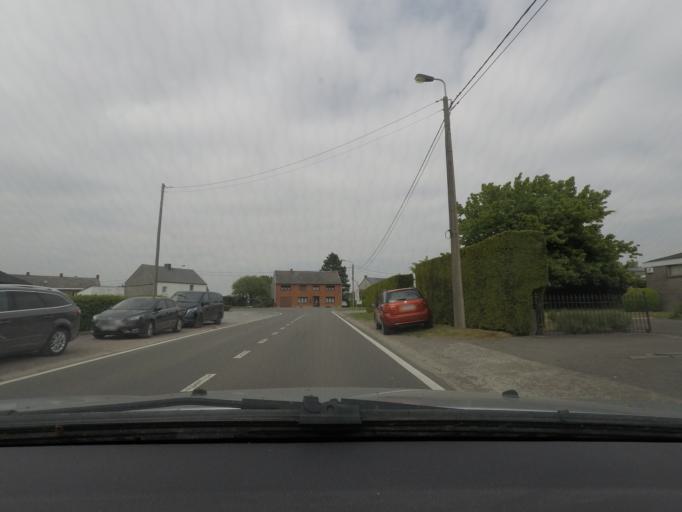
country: BE
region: Wallonia
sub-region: Province de Namur
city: Noville-les-Bois
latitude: 50.5037
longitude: 5.0047
